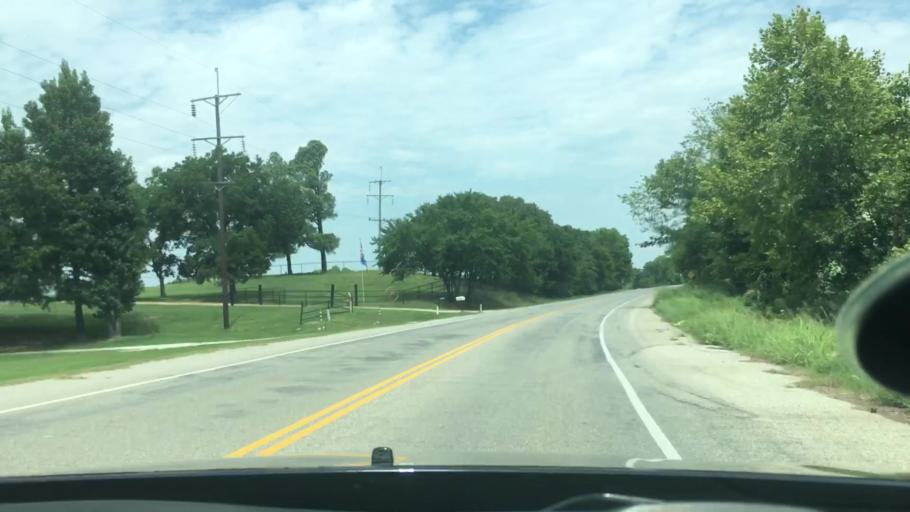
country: US
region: Oklahoma
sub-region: Pontotoc County
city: Byng
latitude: 34.8348
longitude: -96.6791
